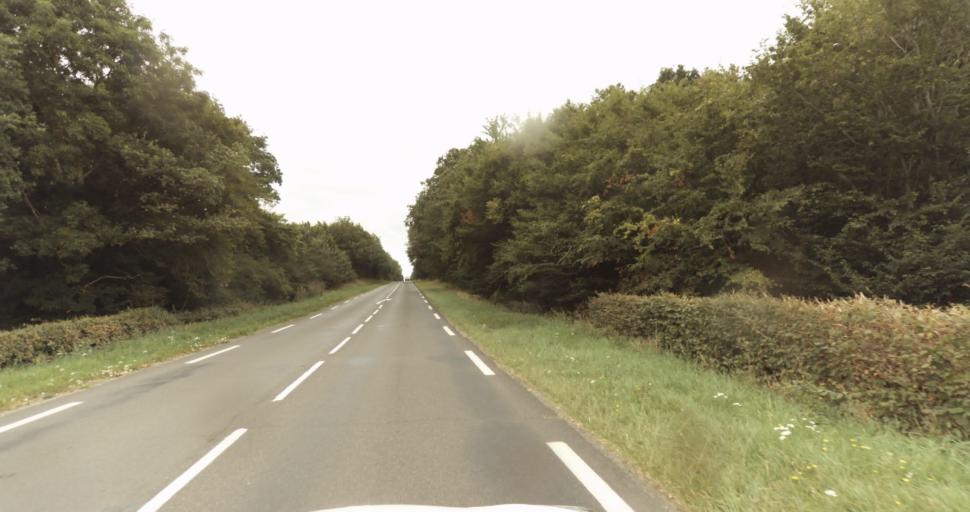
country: FR
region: Haute-Normandie
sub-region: Departement de l'Eure
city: La Madeleine-de-Nonancourt
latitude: 48.8150
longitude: 1.1873
